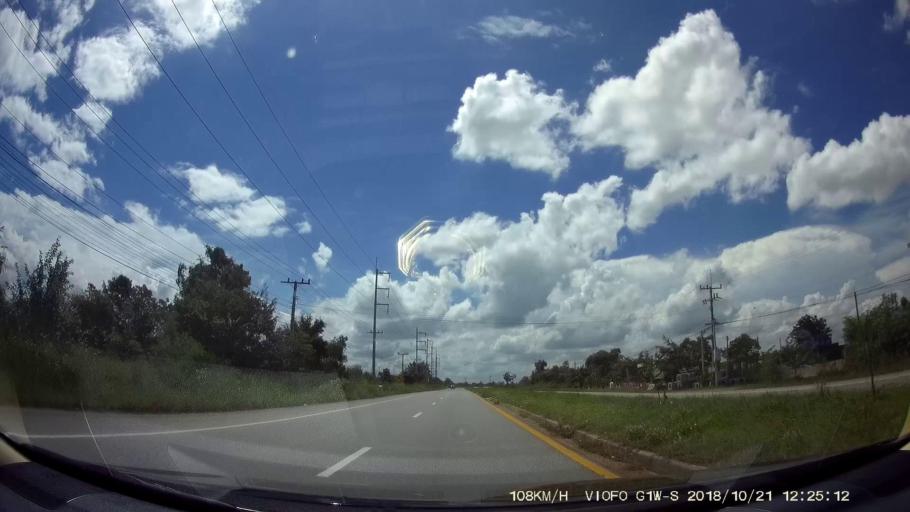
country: TH
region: Nakhon Ratchasima
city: Dan Khun Thot
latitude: 15.2244
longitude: 101.7742
